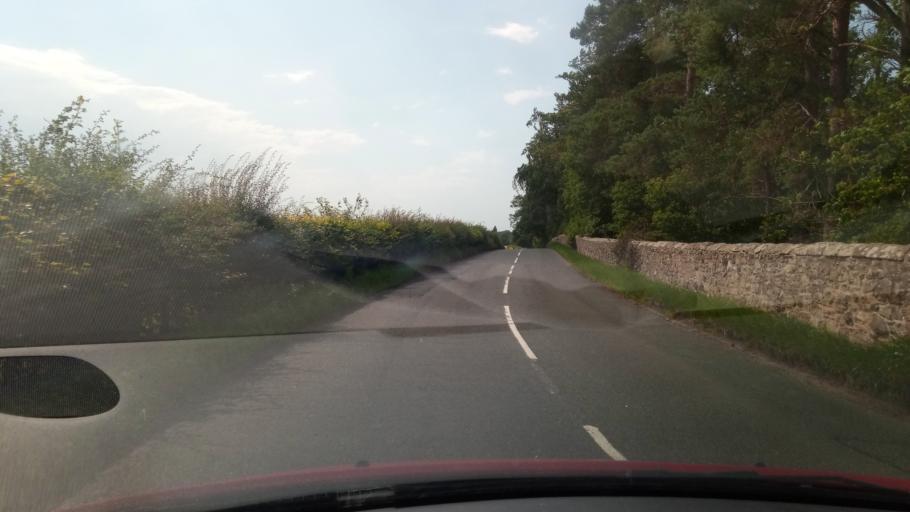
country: GB
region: Scotland
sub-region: The Scottish Borders
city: Kelso
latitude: 55.5913
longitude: -2.4694
